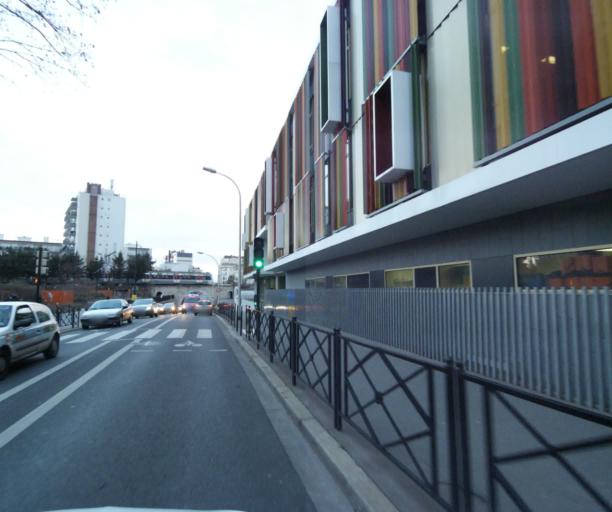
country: FR
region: Ile-de-France
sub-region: Departement des Hauts-de-Seine
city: Courbevoie
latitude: 48.9002
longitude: 2.2565
